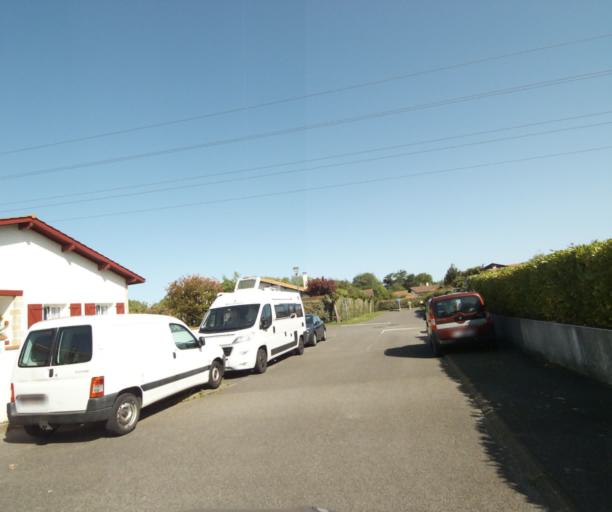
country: FR
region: Aquitaine
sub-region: Departement des Pyrenees-Atlantiques
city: Mouguerre
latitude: 43.4687
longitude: -1.4436
